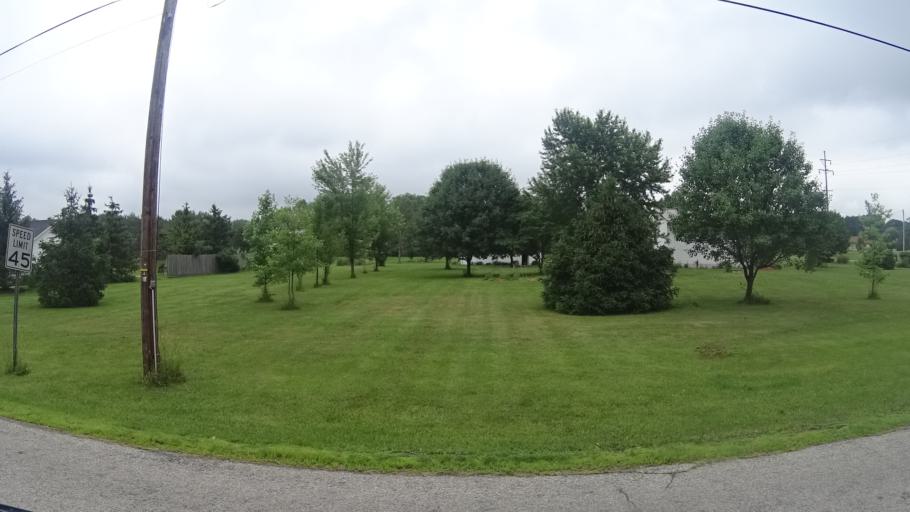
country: US
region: Ohio
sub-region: Erie County
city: Milan
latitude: 41.2864
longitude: -82.5510
